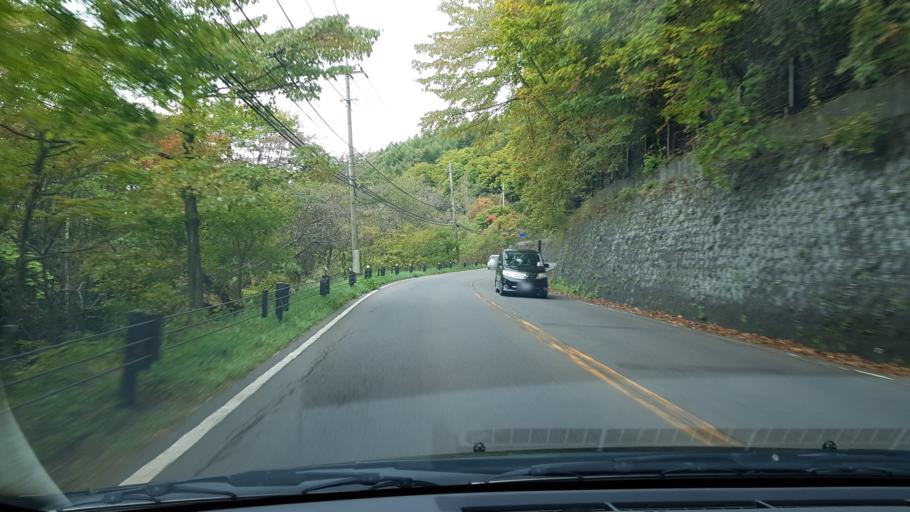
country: JP
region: Nagano
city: Nakano
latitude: 36.6108
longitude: 138.5837
